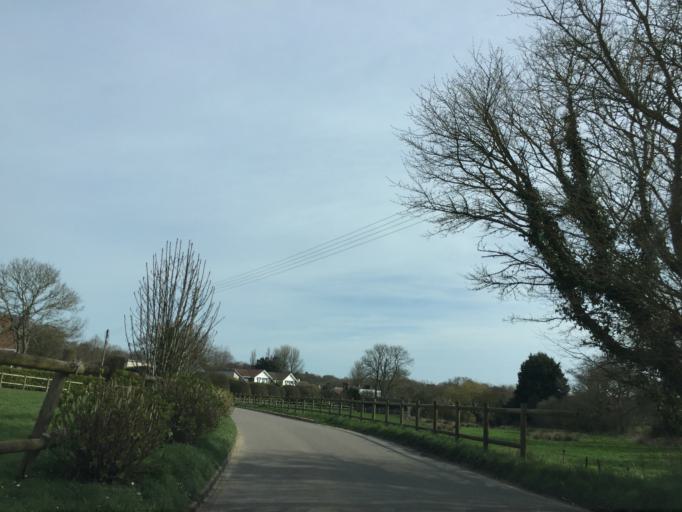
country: JE
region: St Helier
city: Saint Helier
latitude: 49.2311
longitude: -2.1037
